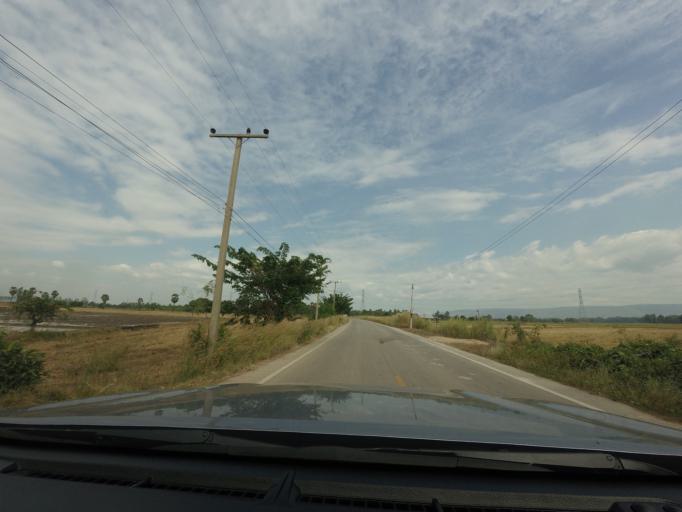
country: TH
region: Phitsanulok
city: Wang Thong
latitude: 16.7380
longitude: 100.3847
